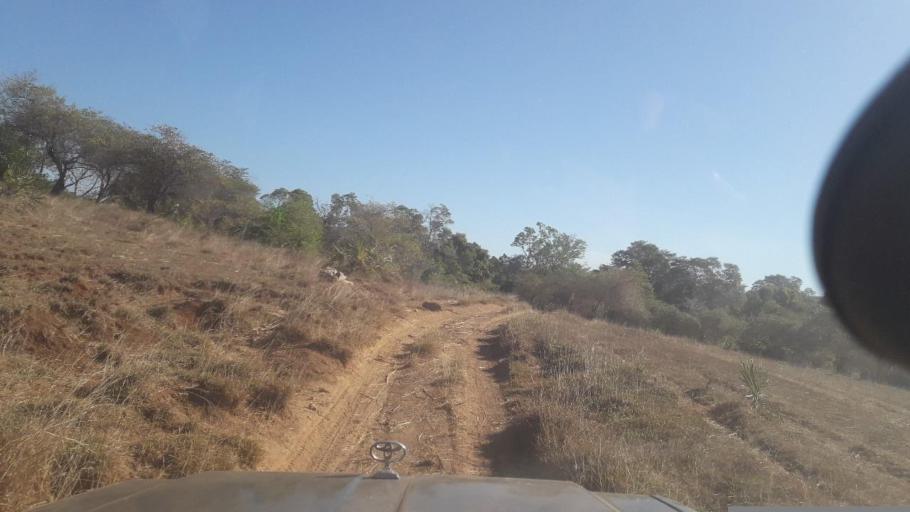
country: MG
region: Boeny
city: Sitampiky
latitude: -16.3766
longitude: 45.5890
